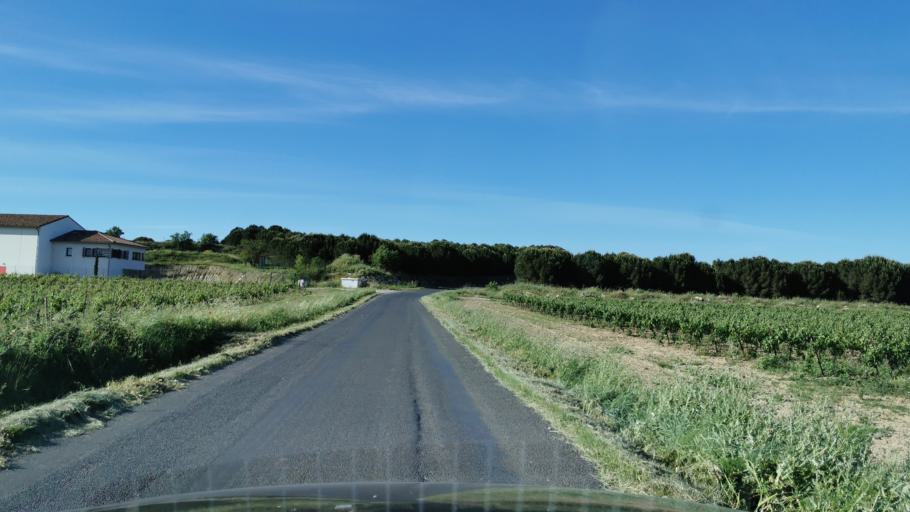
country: FR
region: Languedoc-Roussillon
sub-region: Departement de l'Aude
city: Nevian
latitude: 43.2177
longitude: 2.9127
